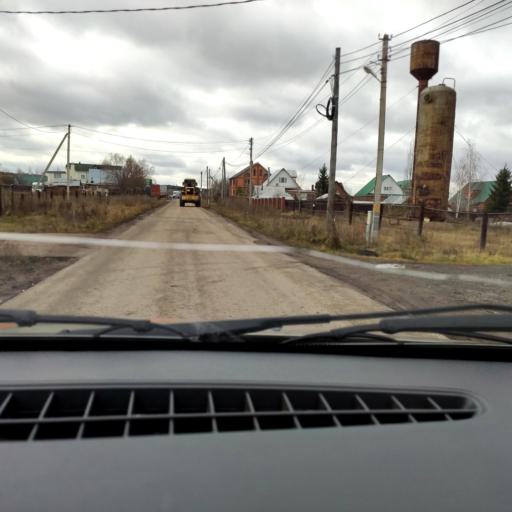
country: RU
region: Bashkortostan
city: Avdon
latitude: 54.4930
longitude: 55.8642
